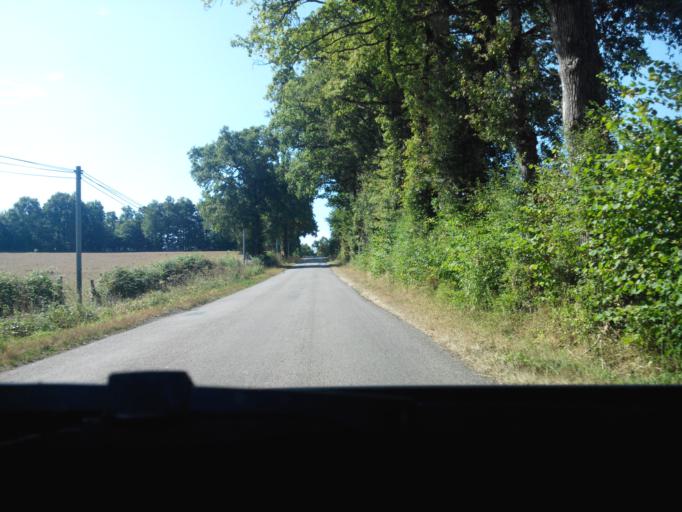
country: FR
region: Poitou-Charentes
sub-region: Departement de la Charente
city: Etagnac
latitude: 45.9597
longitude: 0.7860
